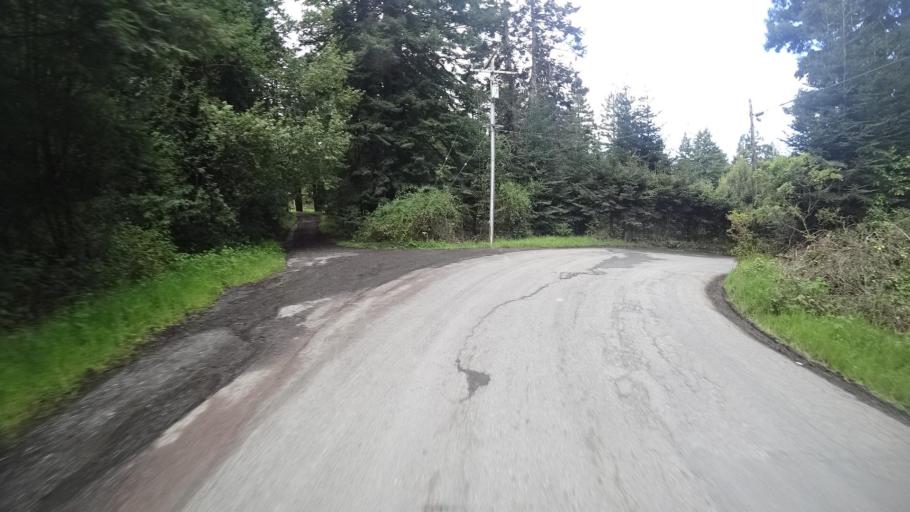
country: US
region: California
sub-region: Humboldt County
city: Blue Lake
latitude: 40.8976
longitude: -124.0007
